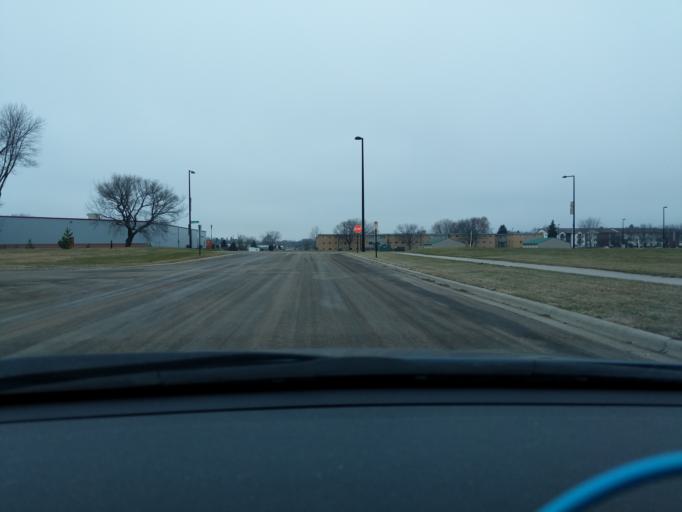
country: US
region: Minnesota
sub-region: Lyon County
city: Marshall
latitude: 44.4516
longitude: -95.7653
